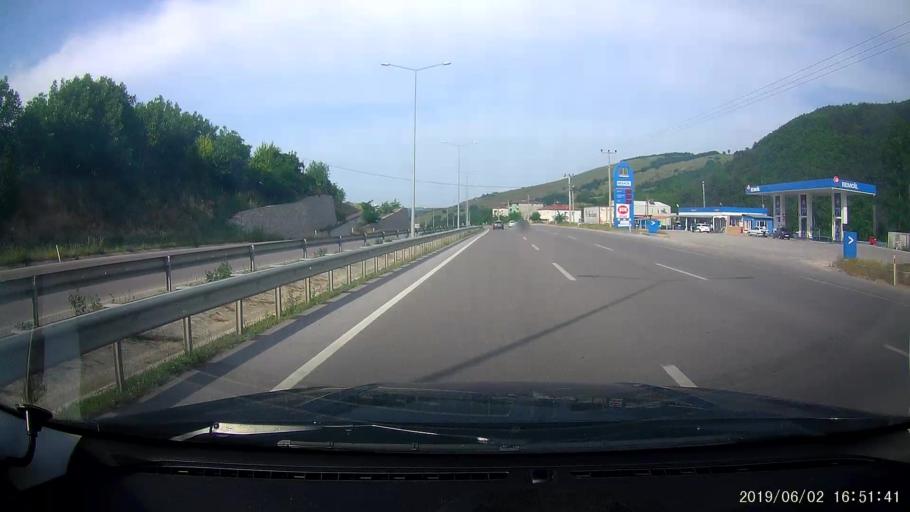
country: TR
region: Samsun
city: Samsun
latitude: 41.2771
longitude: 36.1864
